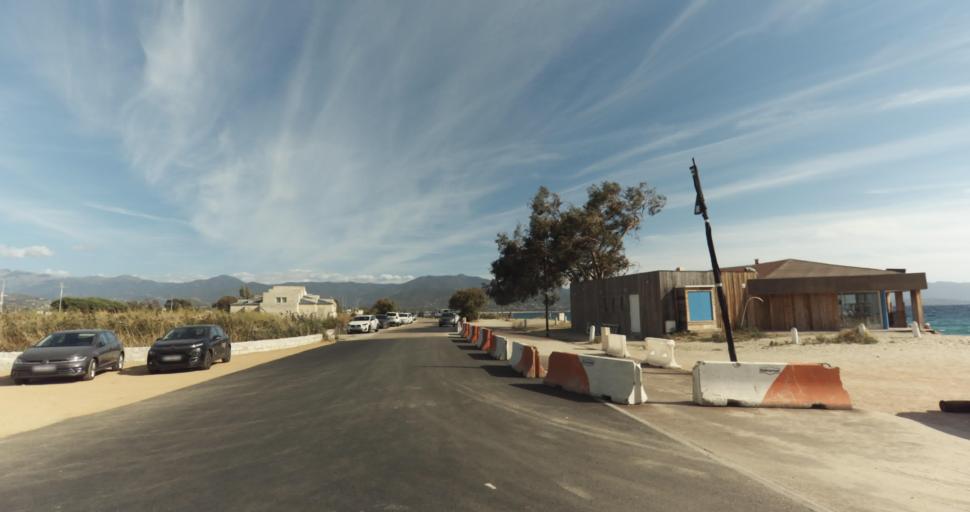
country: FR
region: Corsica
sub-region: Departement de la Corse-du-Sud
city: Ajaccio
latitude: 41.9274
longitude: 8.7759
